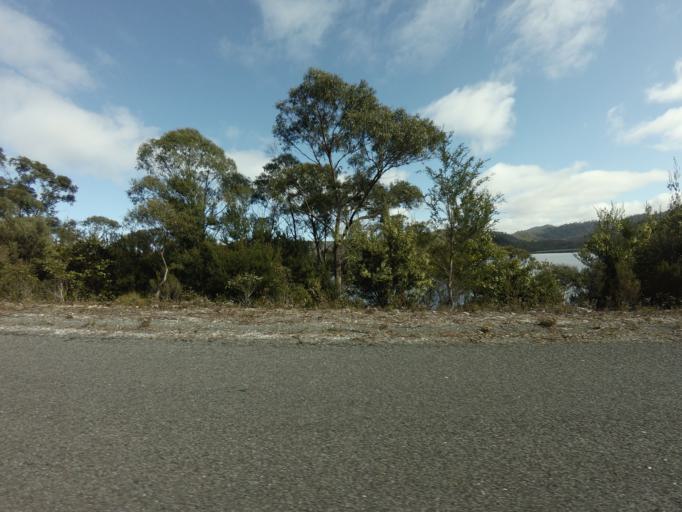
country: AU
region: Tasmania
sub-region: Huon Valley
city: Geeveston
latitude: -42.8311
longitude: 146.1254
